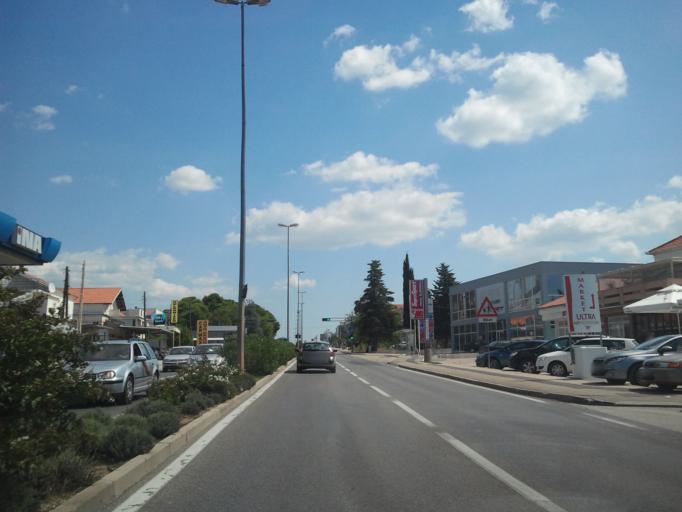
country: HR
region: Zadarska
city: Zadar
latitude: 44.1158
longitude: 15.2601
